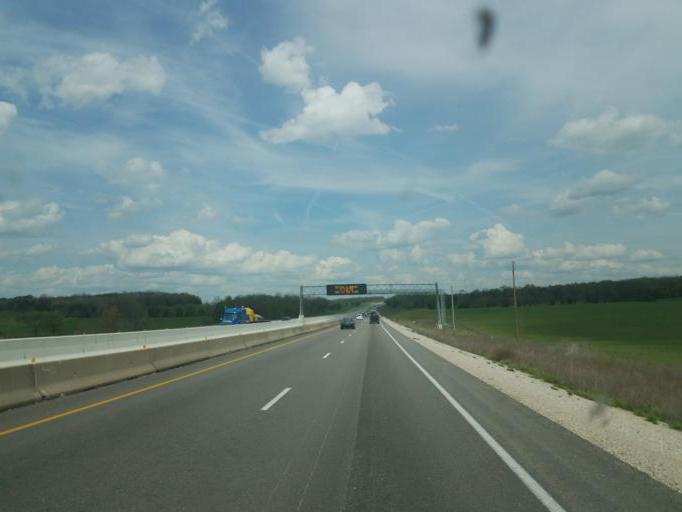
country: US
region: Kentucky
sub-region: Hart County
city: Munfordville
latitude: 37.4265
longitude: -85.8827
